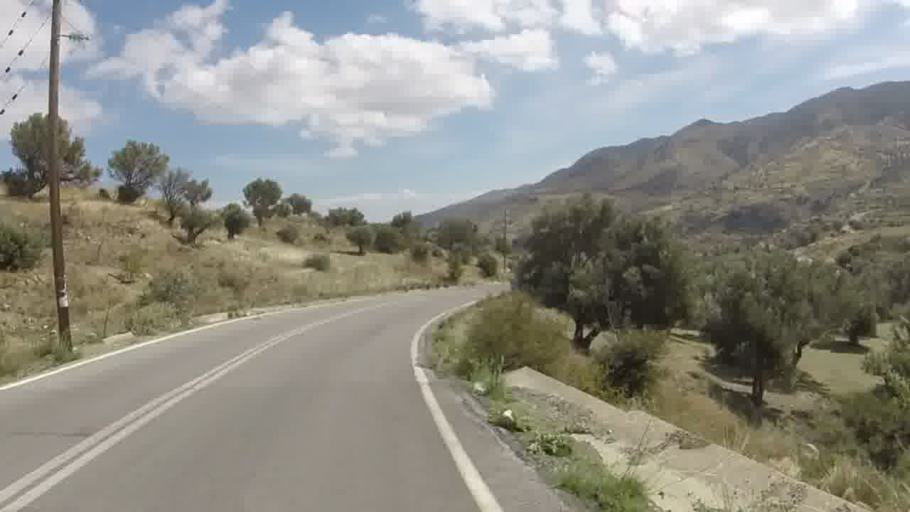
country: GR
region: Crete
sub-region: Nomos Rethymnis
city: Agia Galini
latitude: 35.1482
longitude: 24.6326
